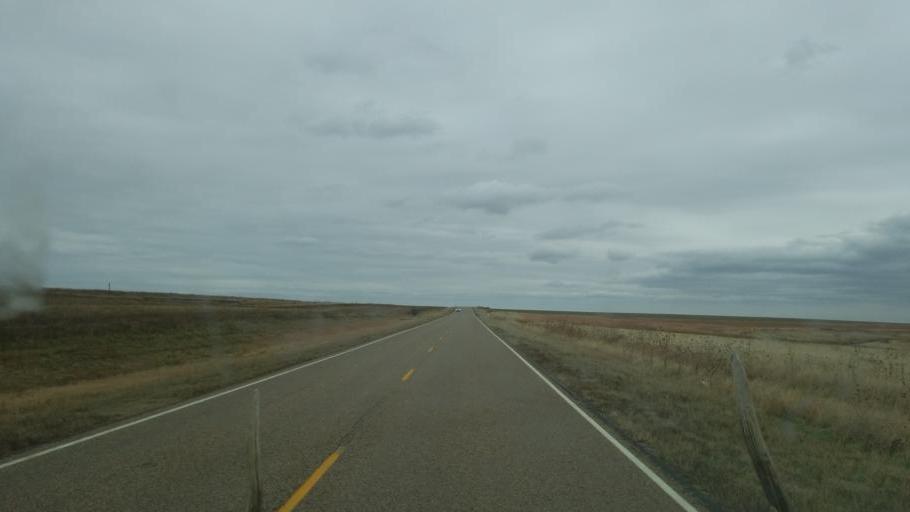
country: US
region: Colorado
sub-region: Cheyenne County
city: Cheyenne Wells
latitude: 38.8482
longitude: -102.1505
